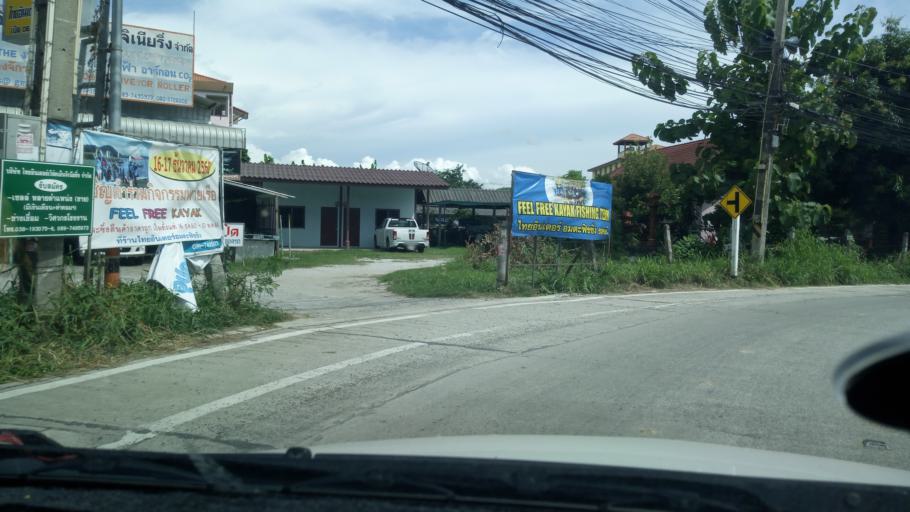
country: TH
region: Chon Buri
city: Chon Buri
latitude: 13.4161
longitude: 101.0289
